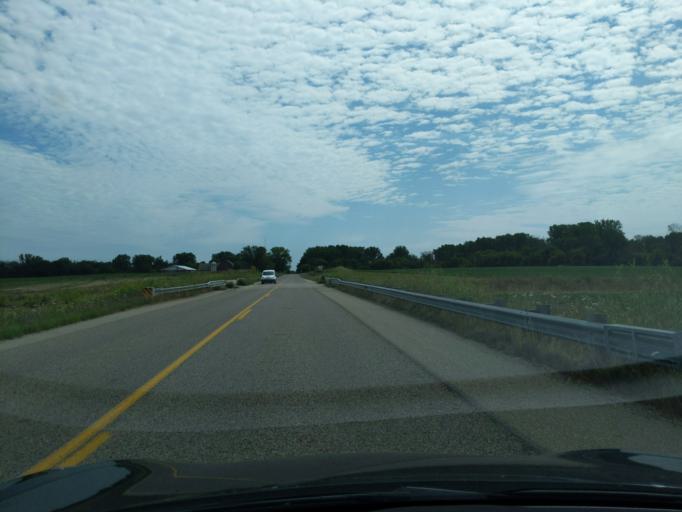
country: US
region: Michigan
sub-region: Gratiot County
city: Breckenridge
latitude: 43.2919
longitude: -84.4221
